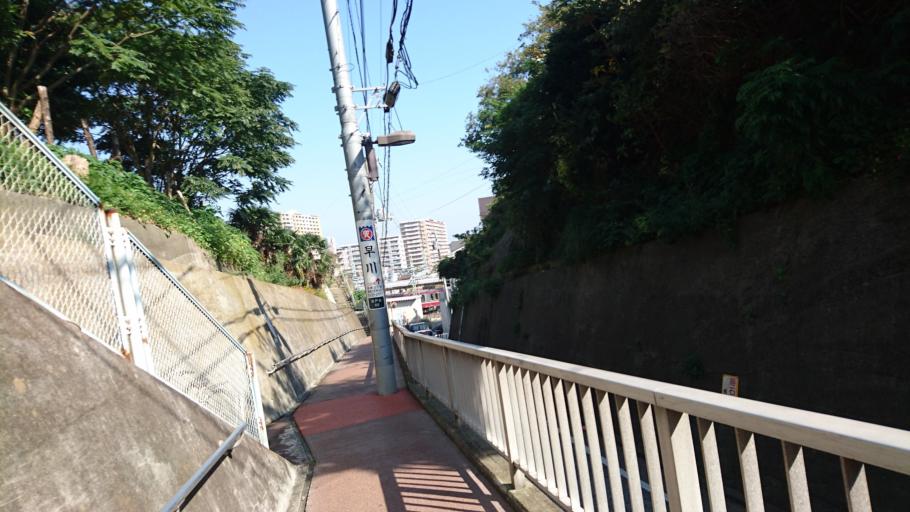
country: JP
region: Kanagawa
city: Yokosuka
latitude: 35.2689
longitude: 139.6768
